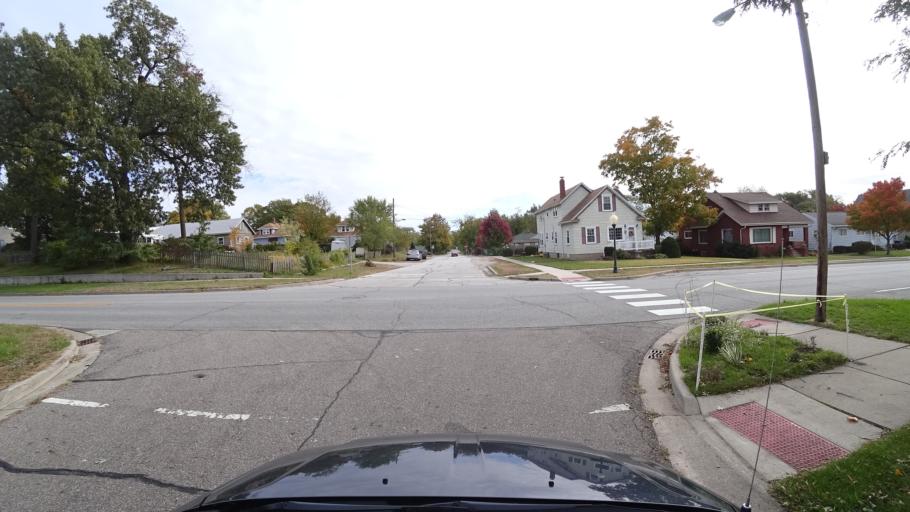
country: US
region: Indiana
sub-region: LaPorte County
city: Michigan City
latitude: 41.7036
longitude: -86.9041
